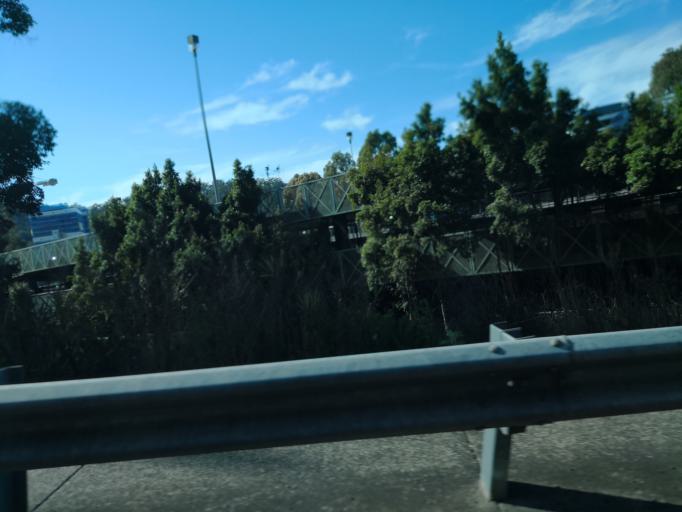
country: AU
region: New South Wales
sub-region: Gosford Shire
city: Gosford
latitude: -33.4255
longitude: 151.3395
